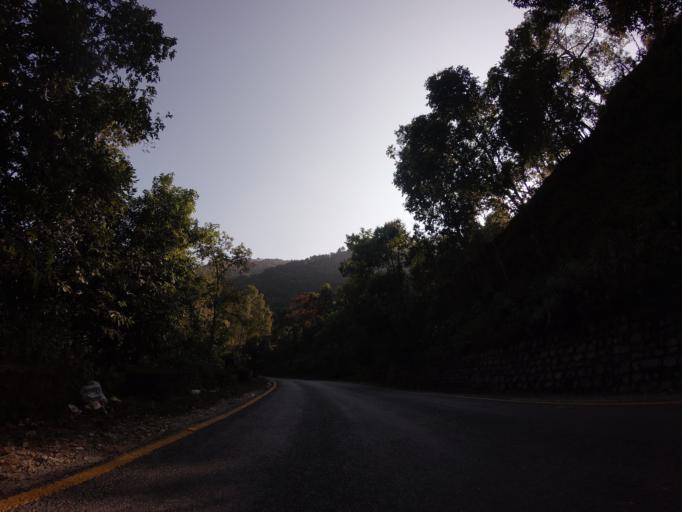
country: NP
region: Western Region
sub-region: Gandaki Zone
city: Pokhara
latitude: 28.1888
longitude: 83.9005
